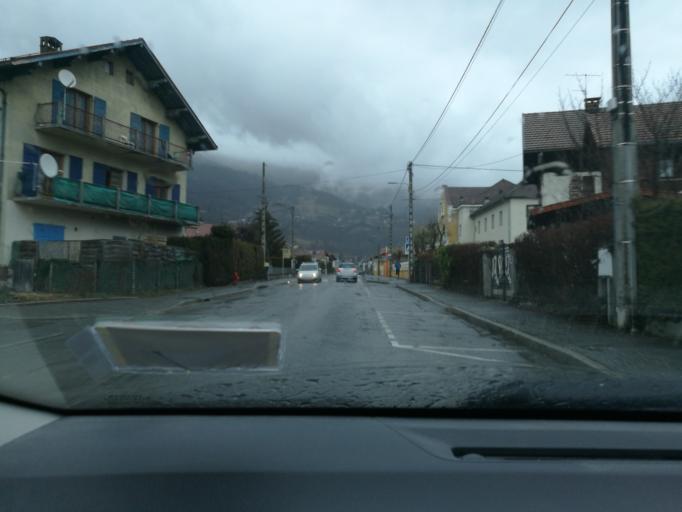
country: FR
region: Rhone-Alpes
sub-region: Departement de la Haute-Savoie
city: Passy
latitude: 45.9224
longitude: 6.7149
